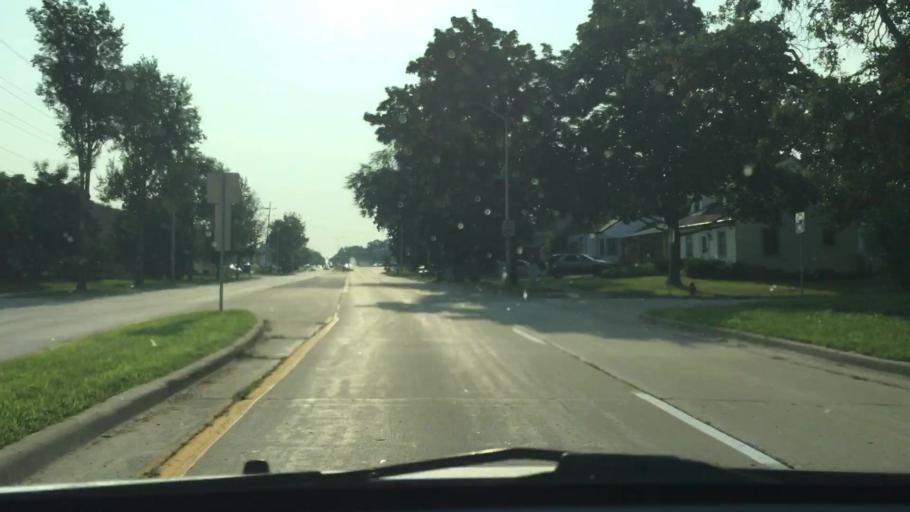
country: US
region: Wisconsin
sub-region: Milwaukee County
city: West Allis
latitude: 42.9954
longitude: -88.0512
